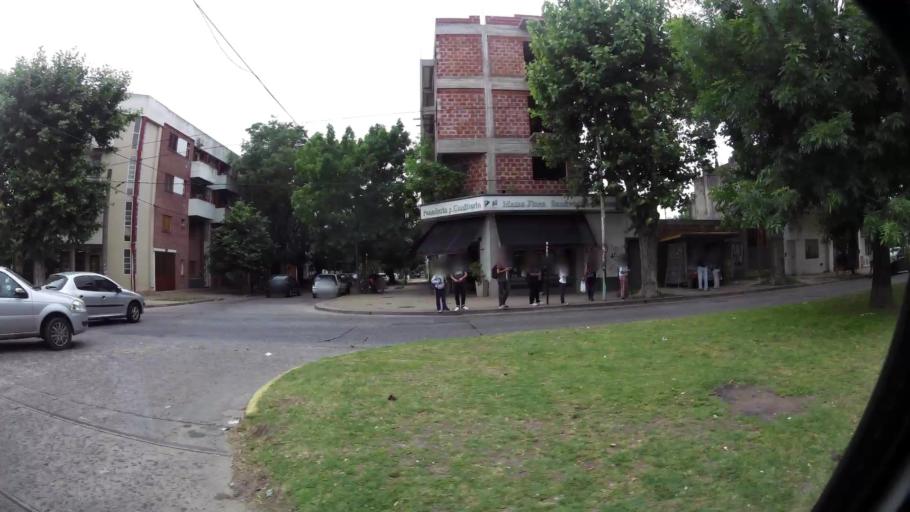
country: AR
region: Buenos Aires
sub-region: Partido de La Plata
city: La Plata
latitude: -34.9351
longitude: -57.9571
